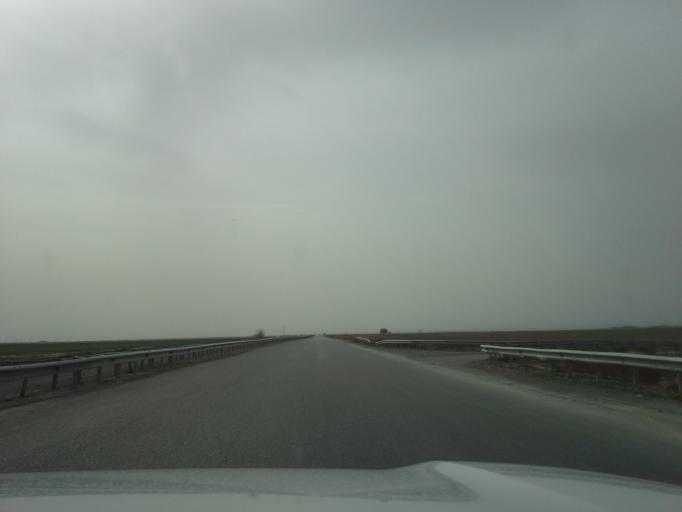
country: TM
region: Ahal
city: Kaka
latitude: 37.4630
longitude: 59.5061
